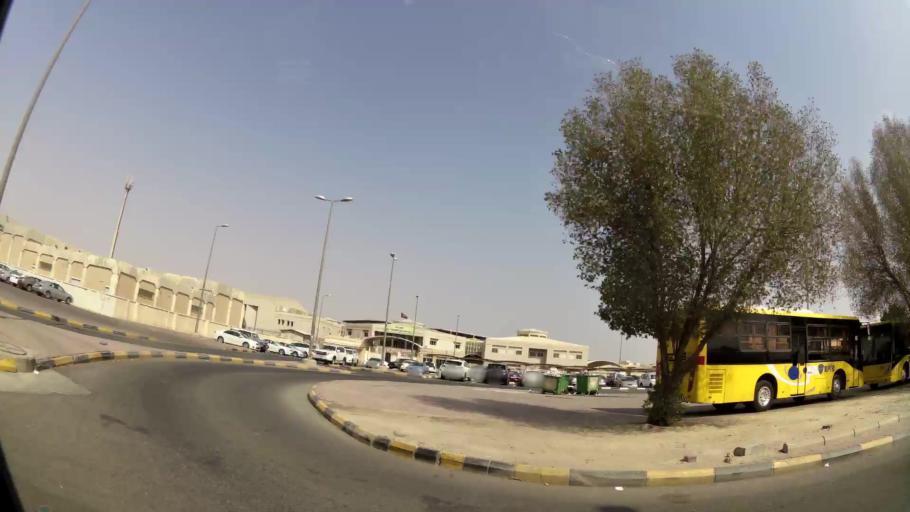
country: KW
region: Muhafazat al Jahra'
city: Al Jahra'
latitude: 29.3397
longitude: 47.6915
